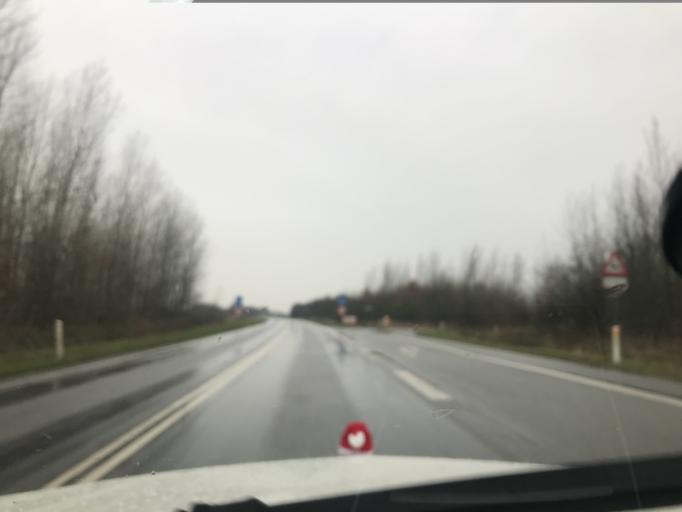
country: DK
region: South Denmark
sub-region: Sonderborg Kommune
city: Grasten
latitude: 54.9882
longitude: 9.6014
